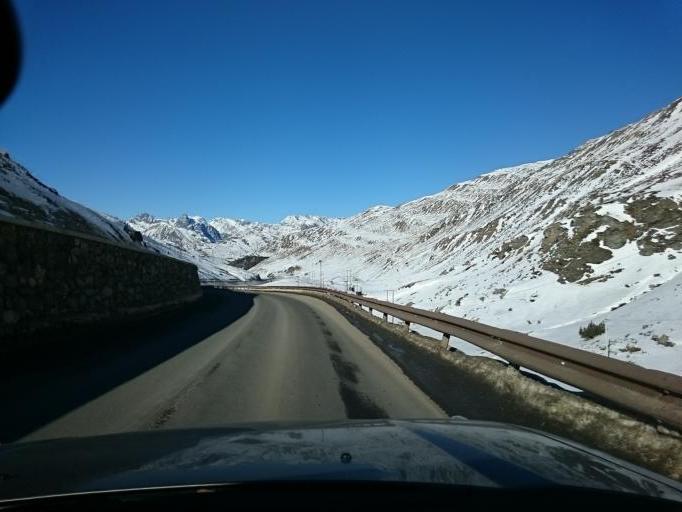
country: IT
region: Lombardy
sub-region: Provincia di Sondrio
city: Livigno
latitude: 46.4991
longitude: 10.2052
